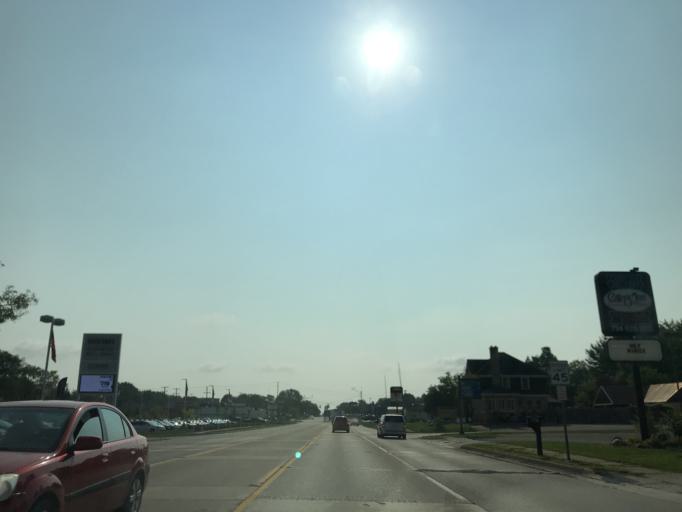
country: US
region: Michigan
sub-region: Washtenaw County
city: Ypsilanti
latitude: 42.2491
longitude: -83.6509
